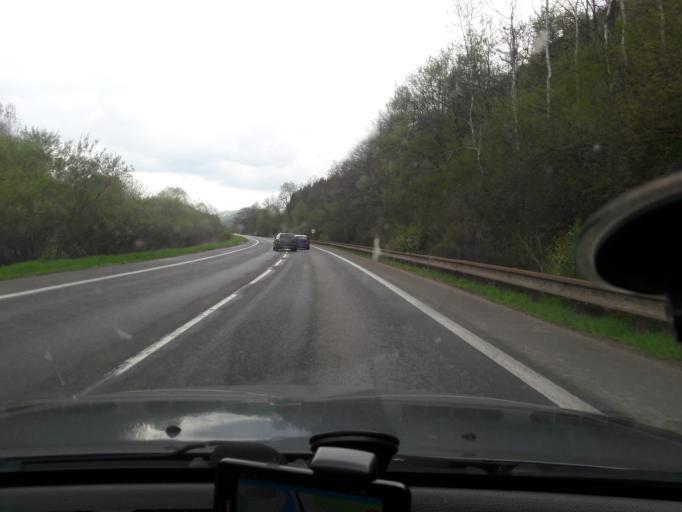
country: SK
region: Banskobystricky
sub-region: Okres Banska Bystrica
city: Brezno
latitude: 48.8118
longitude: 19.6030
